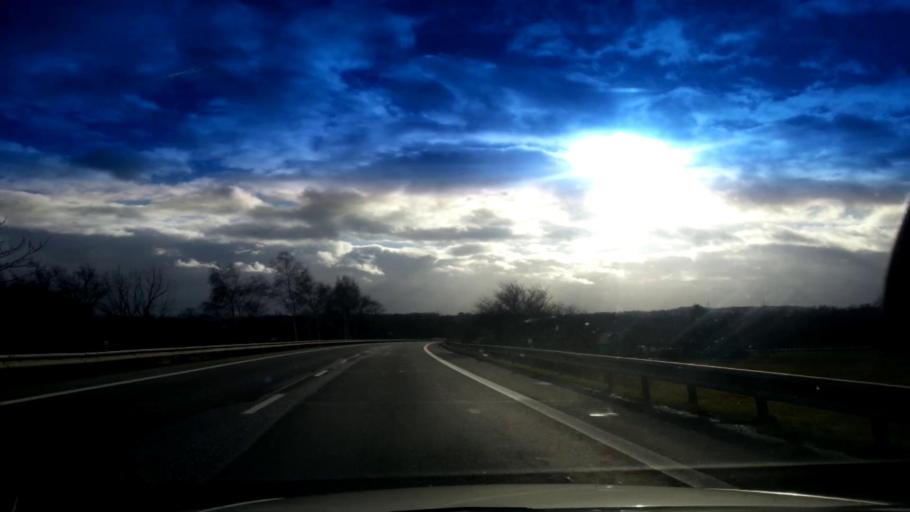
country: CZ
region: Karlovarsky
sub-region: Okres Cheb
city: Frantiskovy Lazne
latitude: 50.1156
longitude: 12.3736
